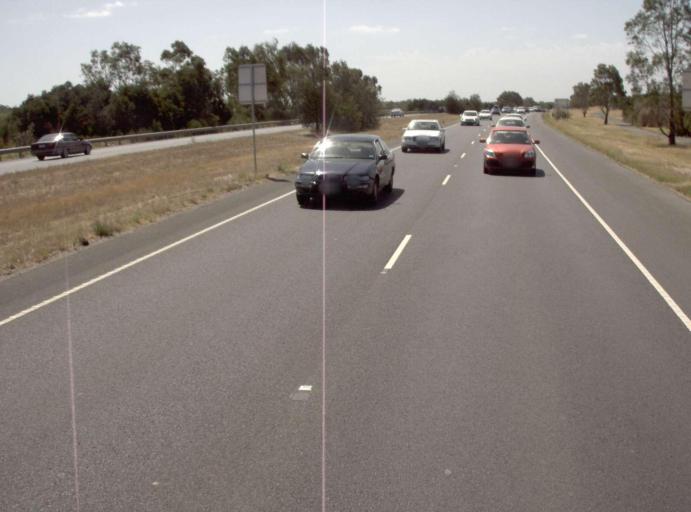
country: AU
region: Victoria
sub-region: Kingston
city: Dingley Village
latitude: -37.9779
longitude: 145.1415
